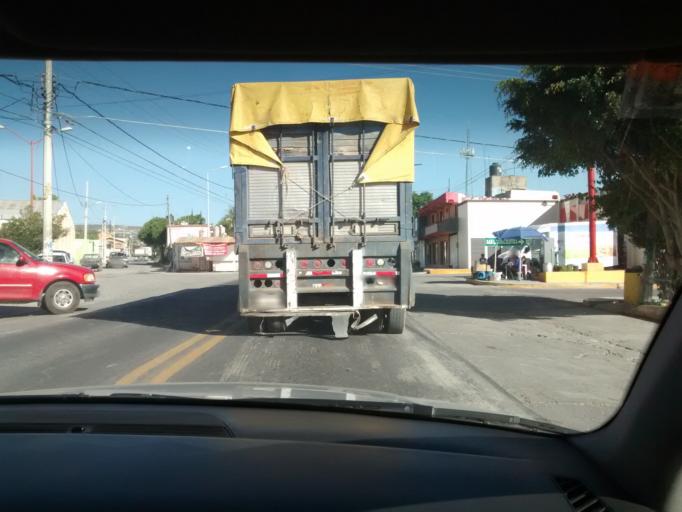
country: MX
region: Puebla
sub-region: Tepanco de Lopez
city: San Andres Cacaloapan
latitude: 18.5552
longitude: -97.5611
